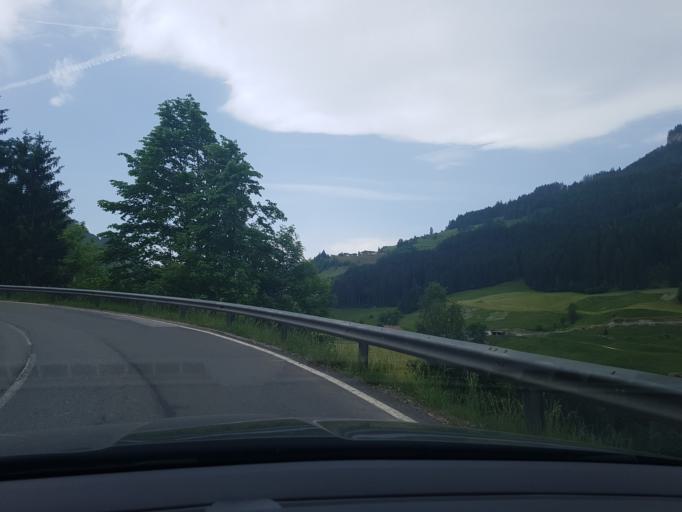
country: AT
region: Salzburg
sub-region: Politischer Bezirk Sankt Johann im Pongau
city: Sankt Johann im Pongau
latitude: 47.2878
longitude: 13.2185
